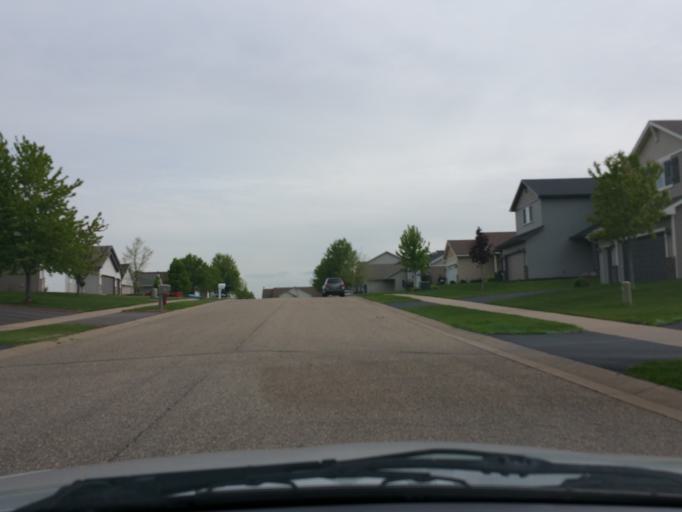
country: US
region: Wisconsin
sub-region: Saint Croix County
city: Hudson
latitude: 44.9532
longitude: -92.6915
